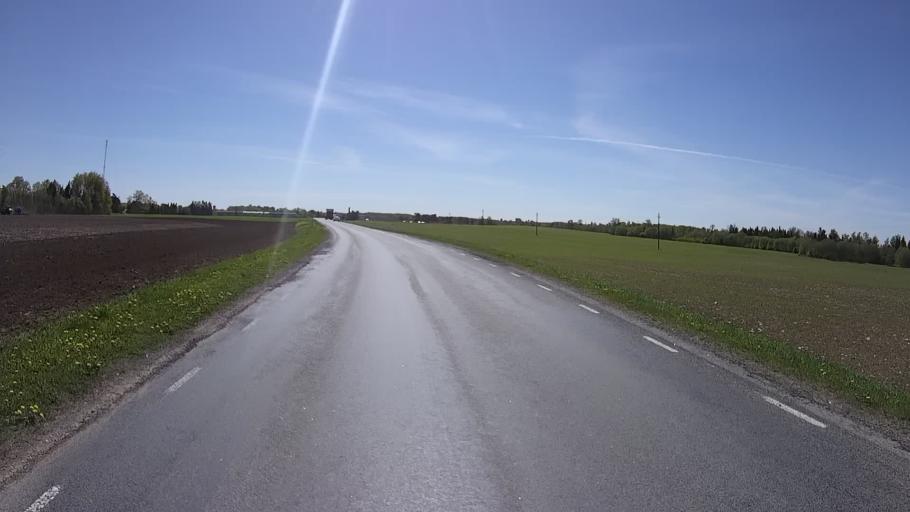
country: EE
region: Harju
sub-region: Raasiku vald
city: Raasiku
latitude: 59.1156
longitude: 25.1686
